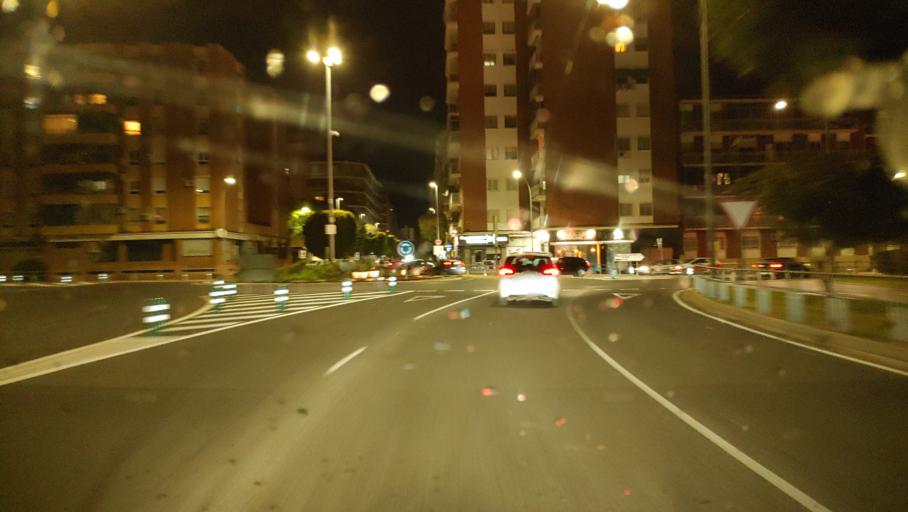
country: ES
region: Castille-La Mancha
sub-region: Provincia de Ciudad Real
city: Ciudad Real
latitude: 38.9863
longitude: -3.9195
